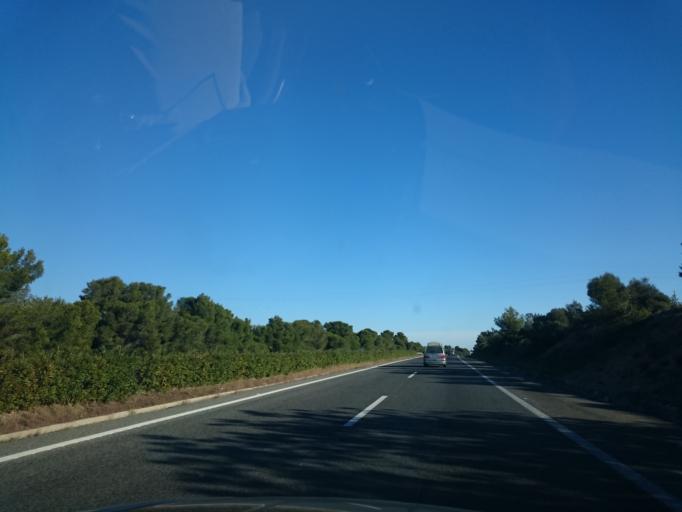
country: ES
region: Catalonia
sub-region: Provincia de Tarragona
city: L'Ampolla
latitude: 40.8249
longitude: 0.7277
